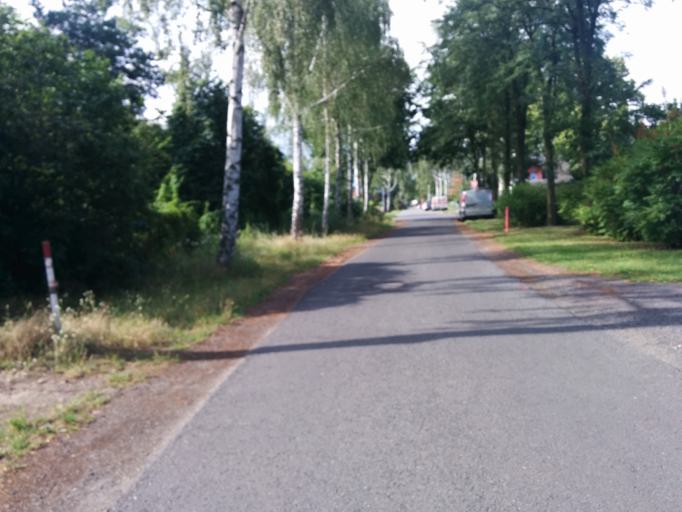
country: DE
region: Berlin
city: Biesdorf
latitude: 52.4845
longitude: 13.5703
